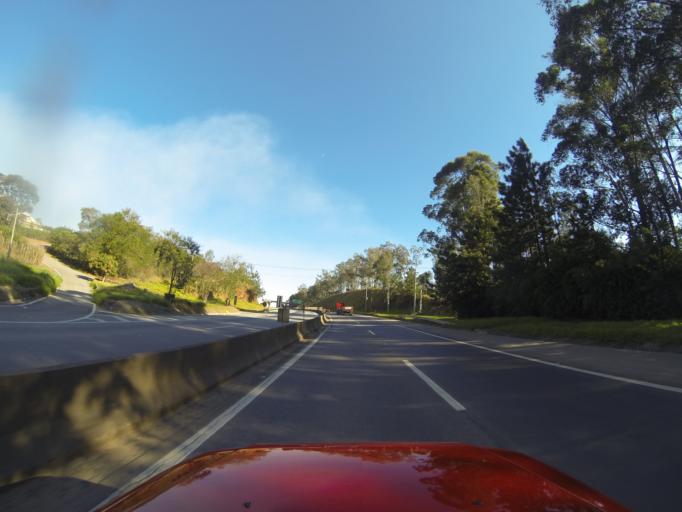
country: BR
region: Sao Paulo
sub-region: Atibaia
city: Atibaia
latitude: -23.0923
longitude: -46.5730
